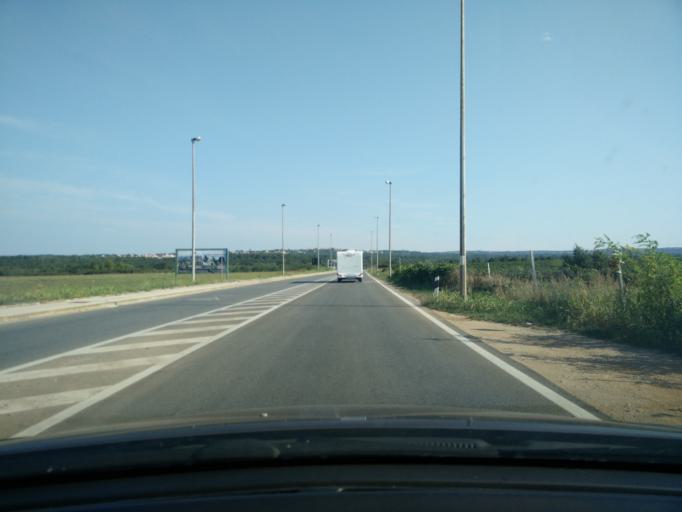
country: HR
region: Istarska
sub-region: Grad Porec
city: Porec
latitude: 45.2696
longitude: 13.6142
